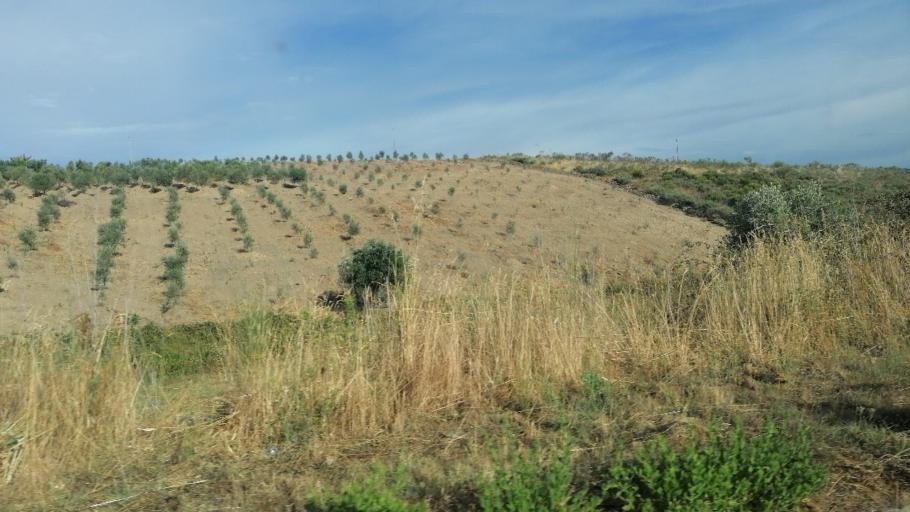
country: PT
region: Viseu
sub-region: Sao Joao da Pesqueira
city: Sao Joao da Pesqueira
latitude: 41.1355
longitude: -7.4381
